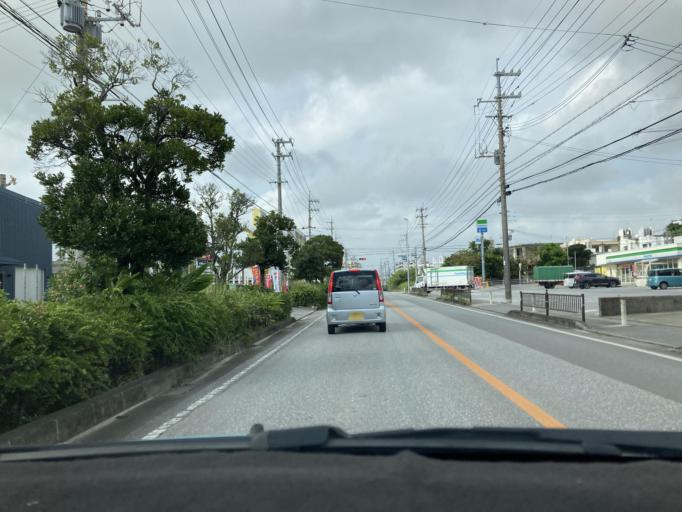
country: JP
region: Okinawa
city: Itoman
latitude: 26.1565
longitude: 127.6708
